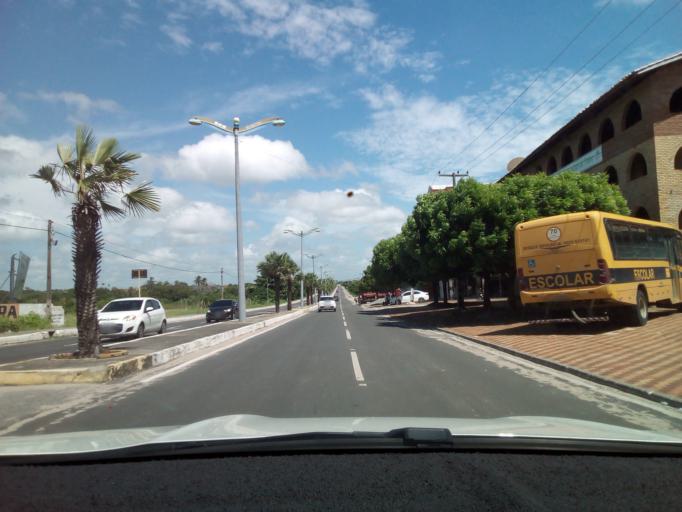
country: BR
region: Ceara
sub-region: Beberibe
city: Beberibe
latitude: -4.1826
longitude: -38.1322
